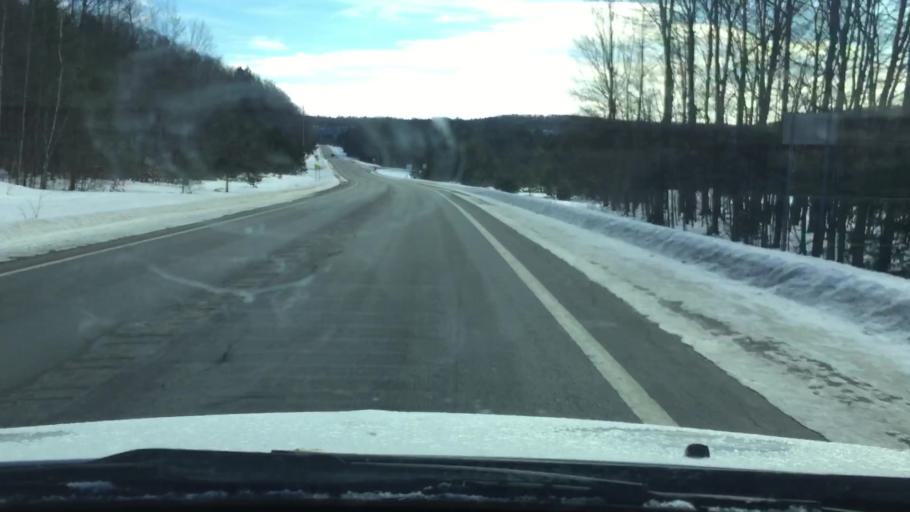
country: US
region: Michigan
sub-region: Antrim County
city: Mancelona
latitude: 44.9702
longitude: -85.0547
